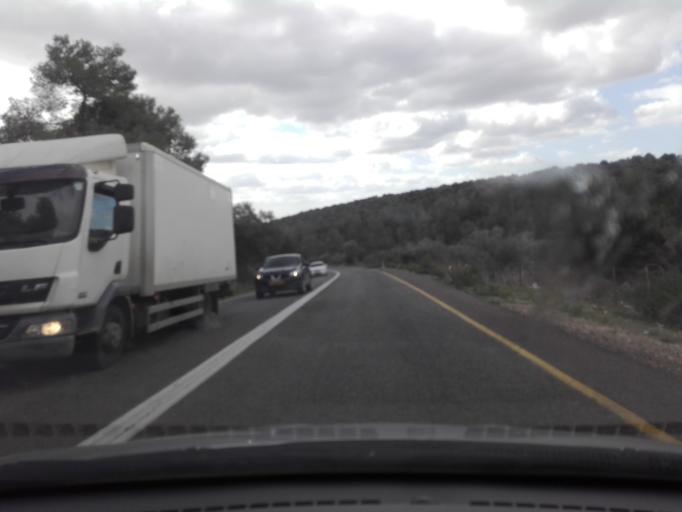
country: IL
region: Haifa
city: Daliyat el Karmil
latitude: 32.6475
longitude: 35.0572
